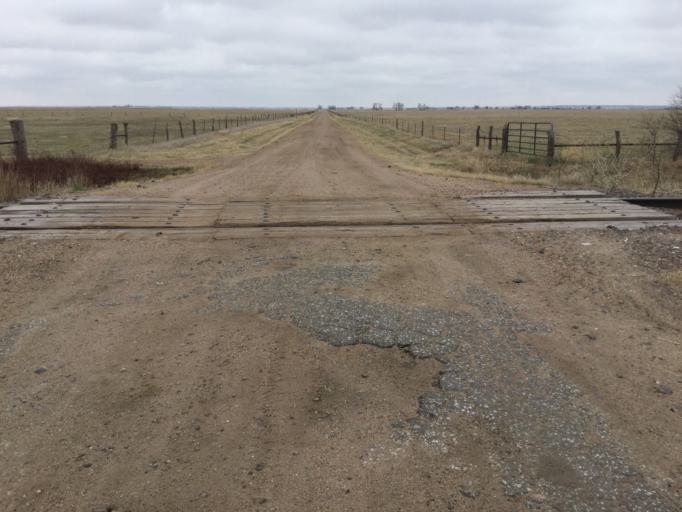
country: US
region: Kansas
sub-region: Barton County
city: Hoisington
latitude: 38.5186
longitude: -98.7382
